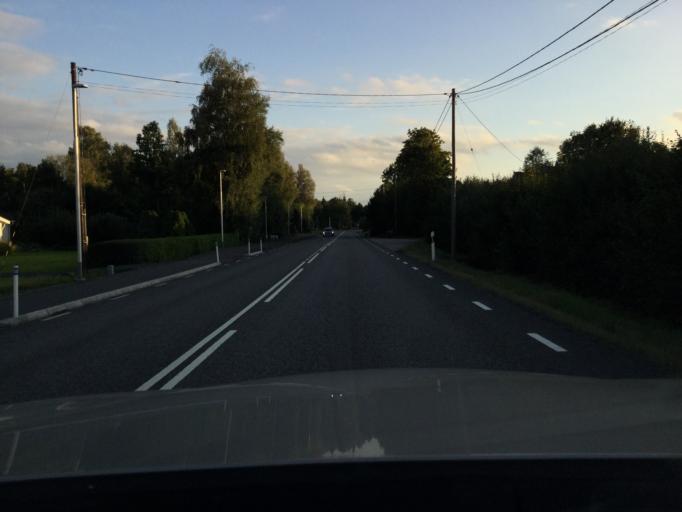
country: SE
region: Kronoberg
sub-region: Almhults Kommun
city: AElmhult
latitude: 56.6597
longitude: 14.2523
